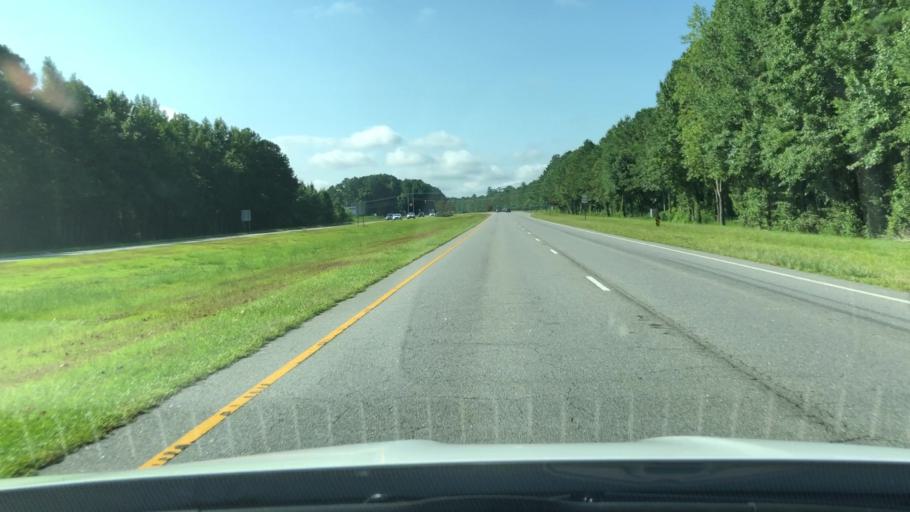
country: US
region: North Carolina
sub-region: Pasquotank County
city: Elizabeth City
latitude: 36.4179
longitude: -76.3418
